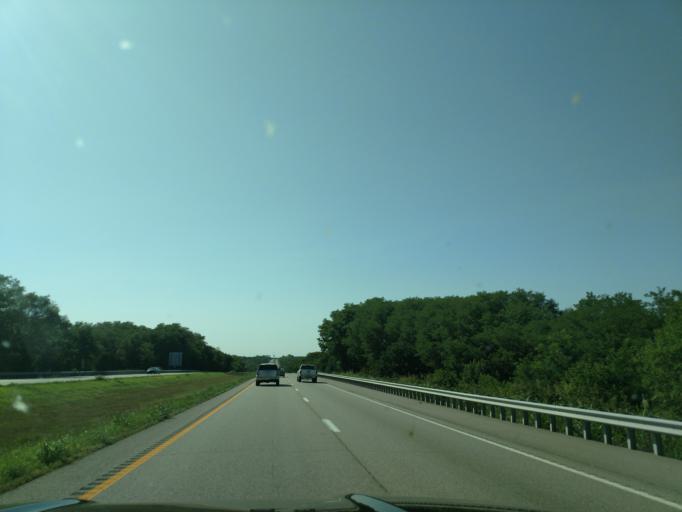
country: US
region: Missouri
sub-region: Andrew County
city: Savannah
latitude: 39.8961
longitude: -94.8722
